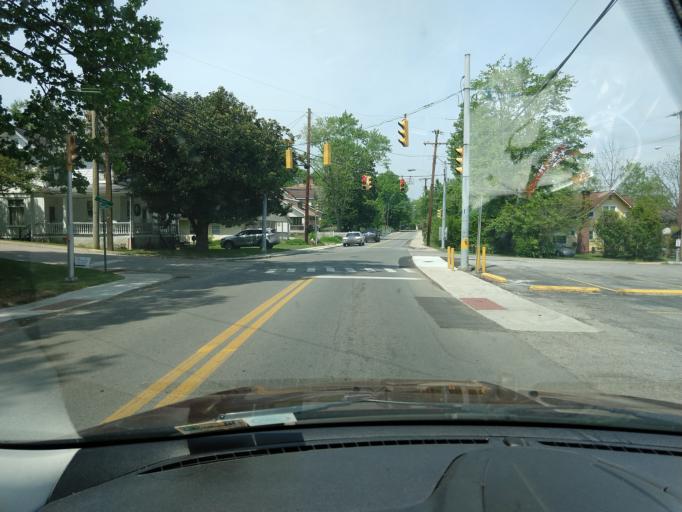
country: US
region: West Virginia
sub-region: Kanawha County
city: Saint Albans
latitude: 38.3812
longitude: -81.8253
